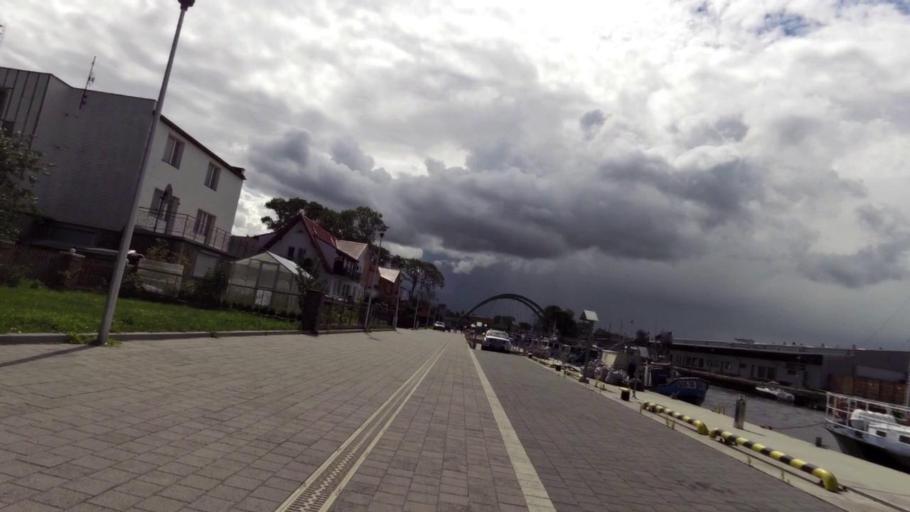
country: PL
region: West Pomeranian Voivodeship
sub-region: Powiat slawienski
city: Darlowo
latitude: 54.4260
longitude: 16.3982
